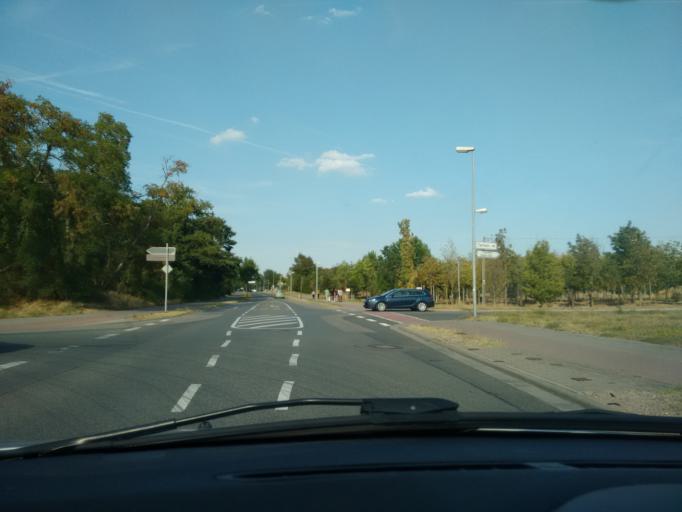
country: DE
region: Rheinland-Pfalz
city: Ingelheim am Rhein
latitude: 49.9849
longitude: 8.0385
